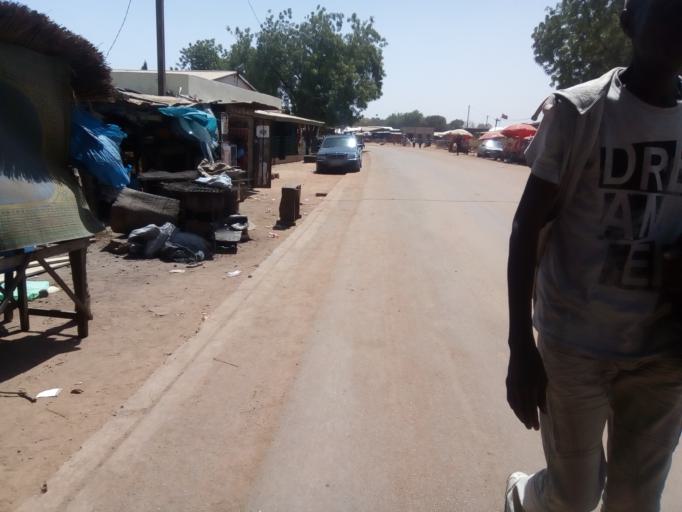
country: GH
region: Upper East
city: Navrongo
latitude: 10.9995
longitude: -1.1152
